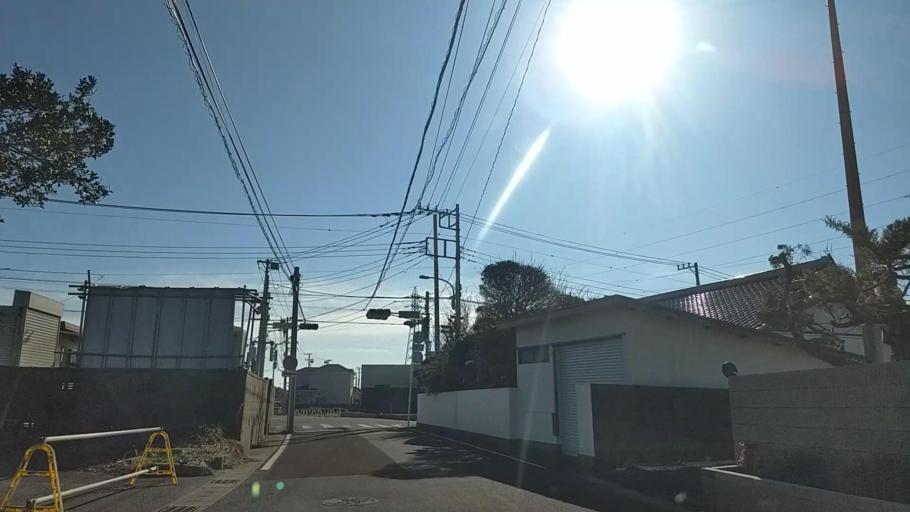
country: JP
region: Chiba
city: Hasaki
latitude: 35.7231
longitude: 140.8424
